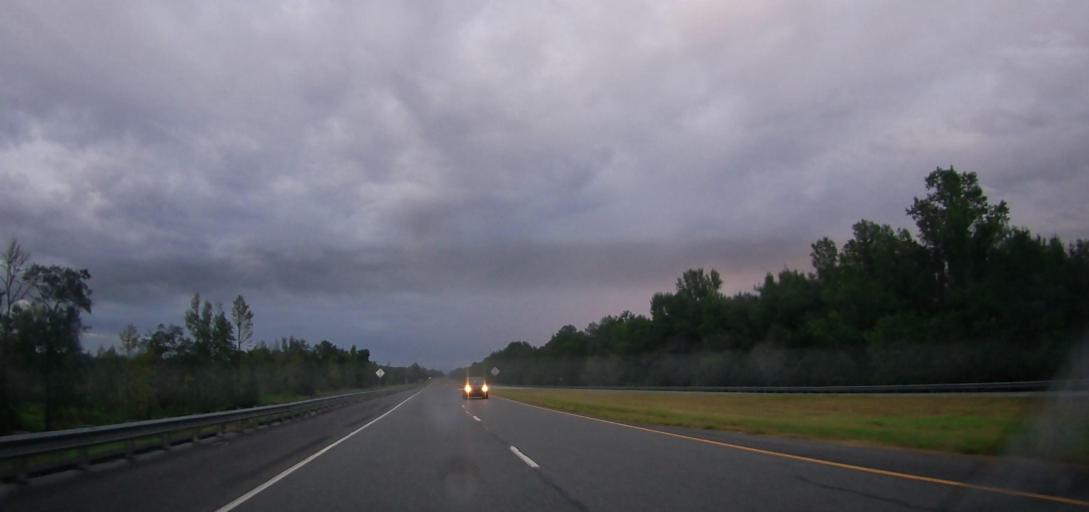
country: US
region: Georgia
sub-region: Lanier County
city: Lakeland
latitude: 30.9268
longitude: -83.0315
